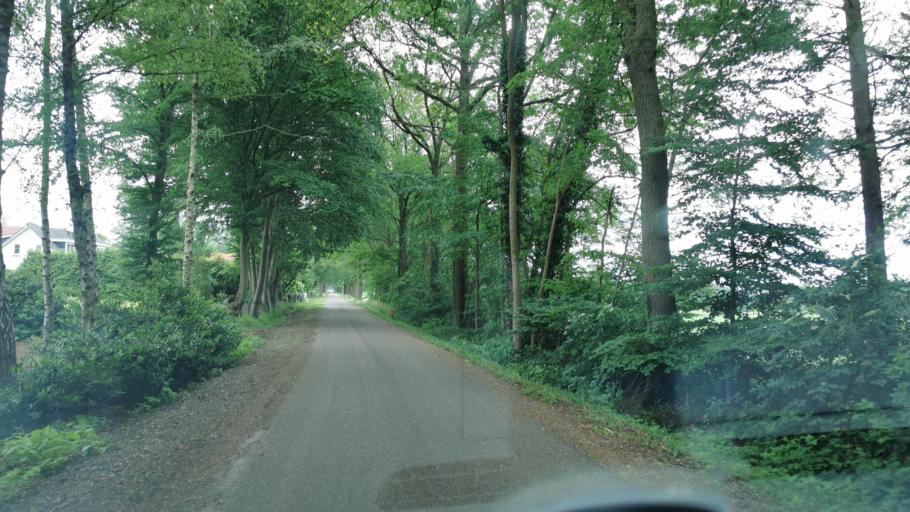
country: DE
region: North Rhine-Westphalia
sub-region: Regierungsbezirk Munster
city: Gronau
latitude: 52.2310
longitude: 7.0196
